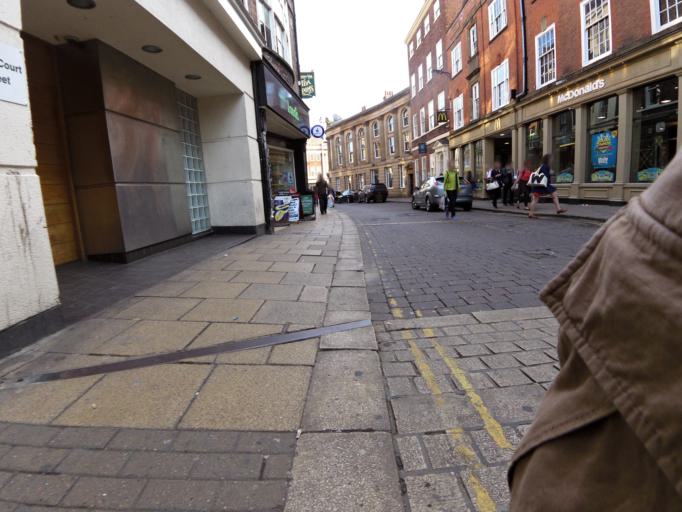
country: GB
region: England
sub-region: City of York
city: York
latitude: 53.9608
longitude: -1.0846
